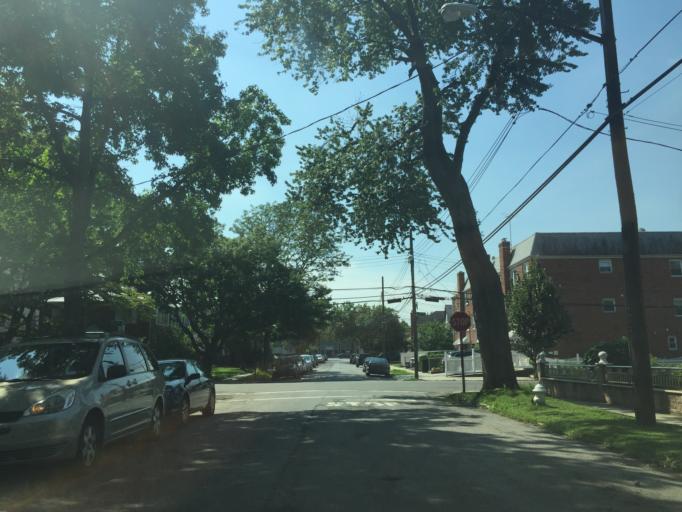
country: US
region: New York
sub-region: Nassau County
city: East Atlantic Beach
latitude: 40.7604
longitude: -73.7754
